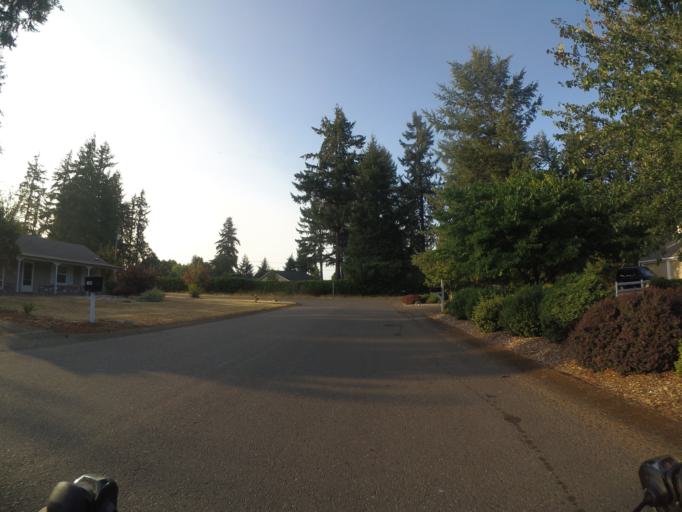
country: US
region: Washington
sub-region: Pierce County
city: Lakewood
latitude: 47.1518
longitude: -122.5185
